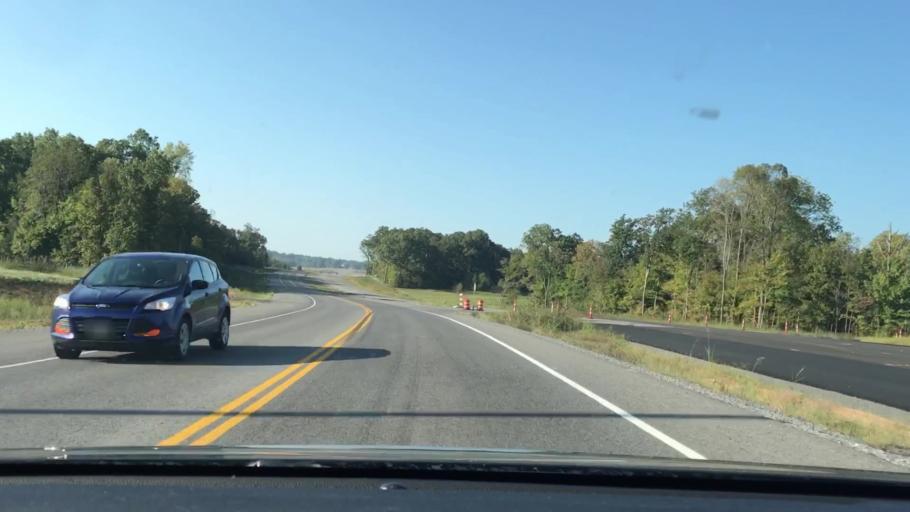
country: US
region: Kentucky
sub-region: Trigg County
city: Cadiz
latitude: 36.8369
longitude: -87.8629
